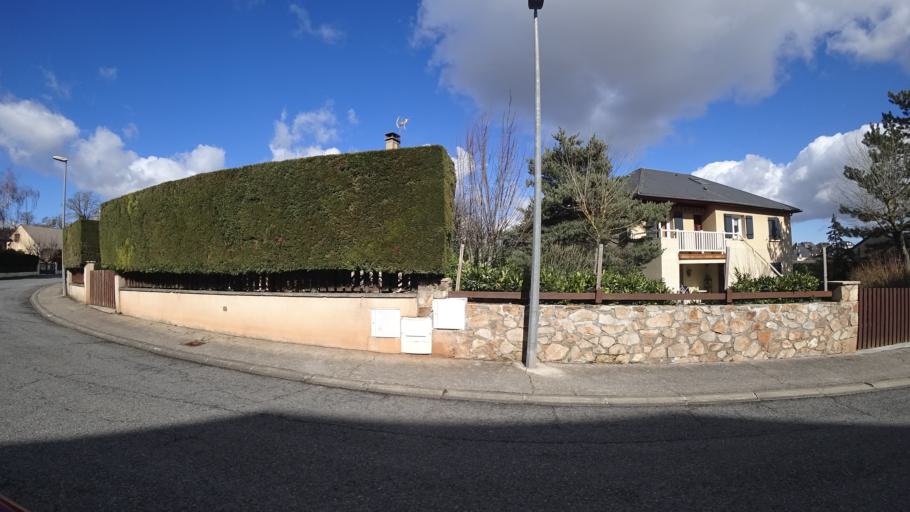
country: FR
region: Midi-Pyrenees
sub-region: Departement de l'Aveyron
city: Olemps
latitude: 44.3661
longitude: 2.5569
